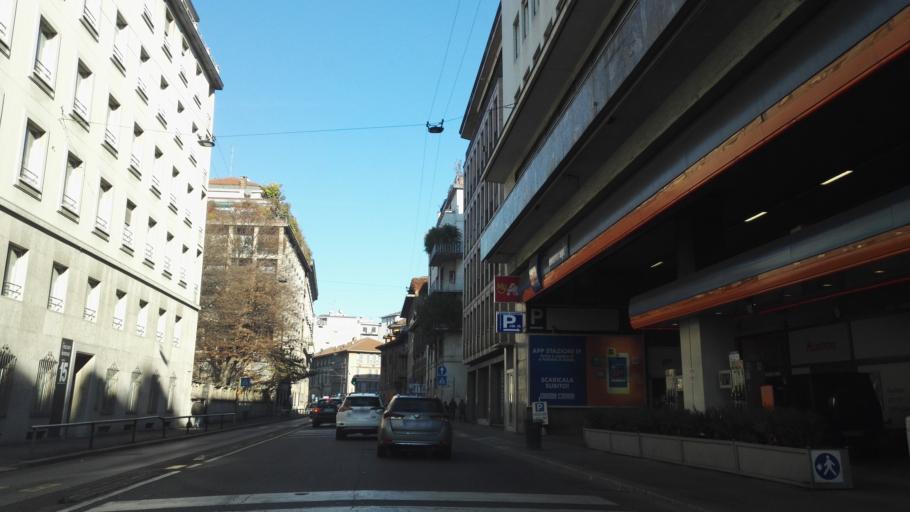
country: IT
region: Lombardy
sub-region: Citta metropolitana di Milano
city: Milano
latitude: 45.4643
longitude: 9.1998
